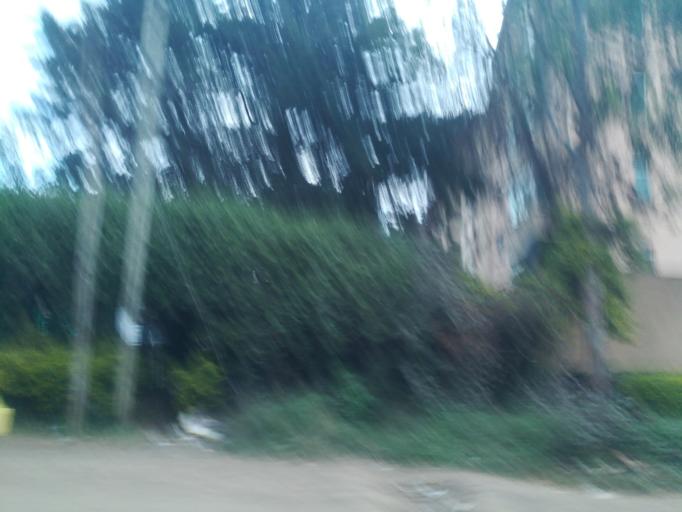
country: KE
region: Nairobi Area
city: Nairobi
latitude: -1.2912
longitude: 36.7906
